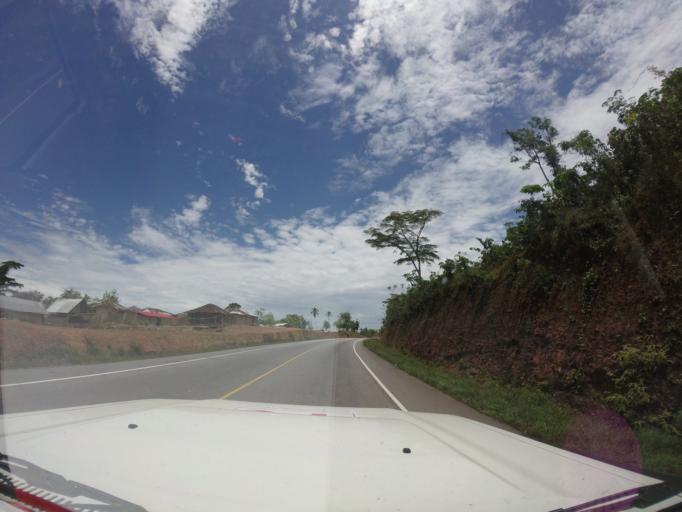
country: LR
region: Bong
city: Gbarnga
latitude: 6.8201
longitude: -9.8883
